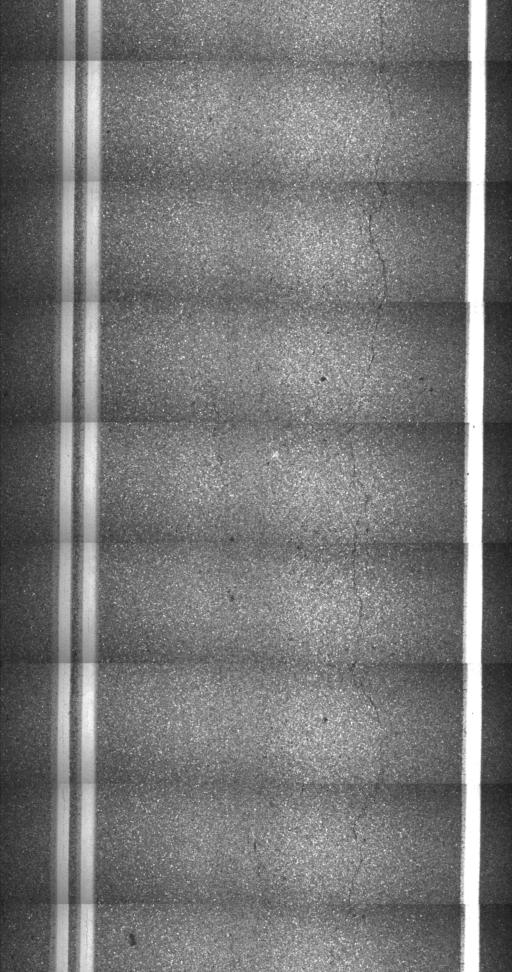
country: US
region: Massachusetts
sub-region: Berkshire County
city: Williamstown
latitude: 42.7707
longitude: -73.2399
